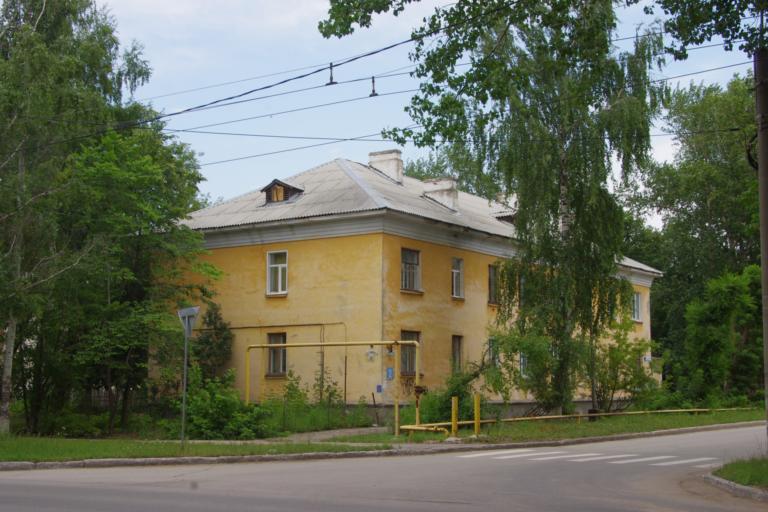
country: RU
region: Samara
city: Tol'yatti
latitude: 53.5042
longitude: 49.3903
